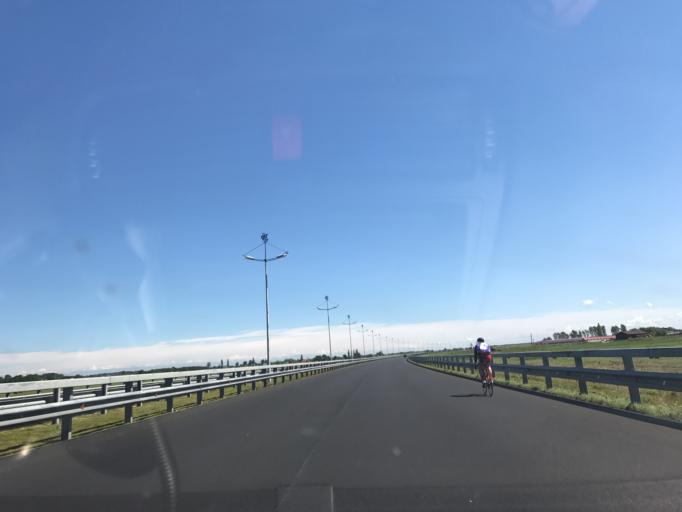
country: RU
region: Kaliningrad
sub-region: Zelenogradskiy Rayon
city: Zelenogradsk
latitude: 54.9202
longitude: 20.4555
